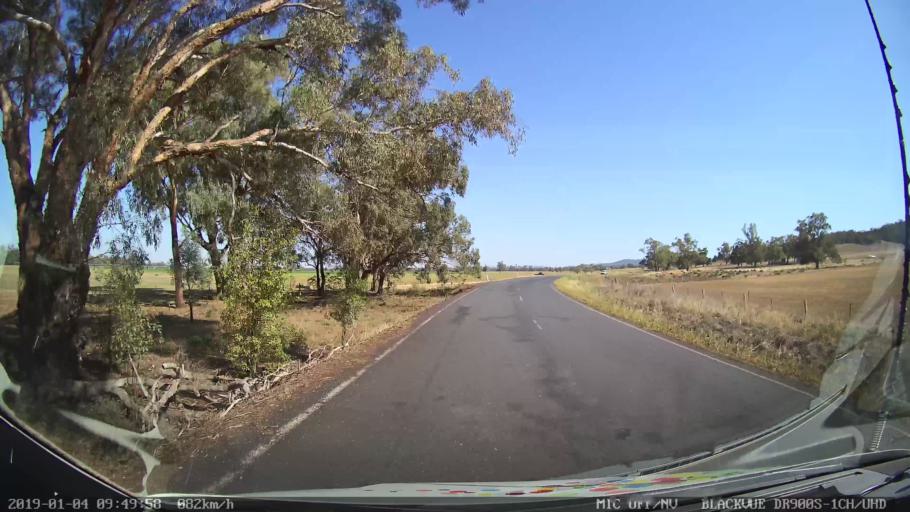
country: AU
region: New South Wales
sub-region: Cabonne
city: Canowindra
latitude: -33.5897
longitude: 148.4151
